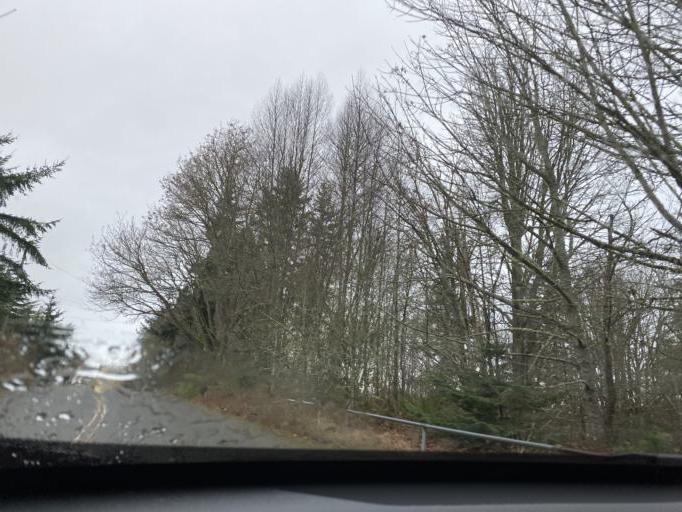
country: US
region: Washington
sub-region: King County
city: Seattle
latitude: 47.6619
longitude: -122.4137
